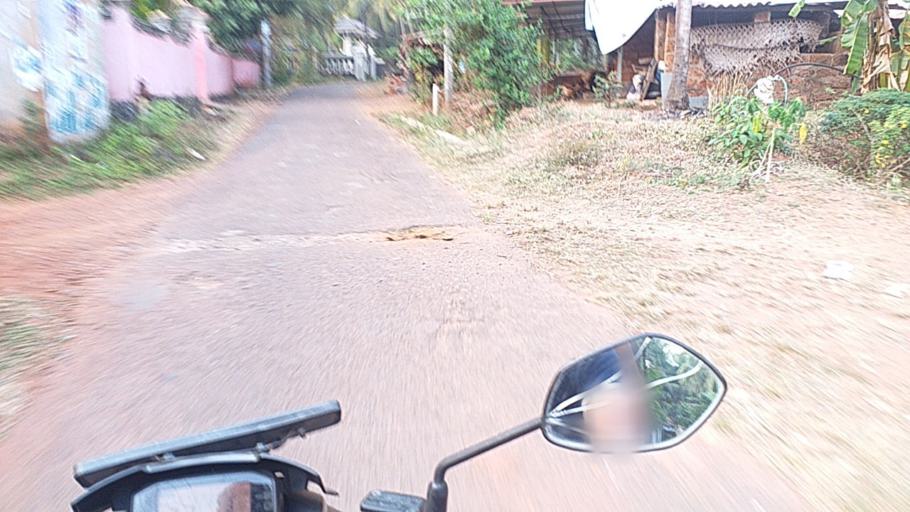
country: IN
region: Kerala
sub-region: Thrissur District
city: Kunnamkulam
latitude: 10.7418
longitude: 76.0413
